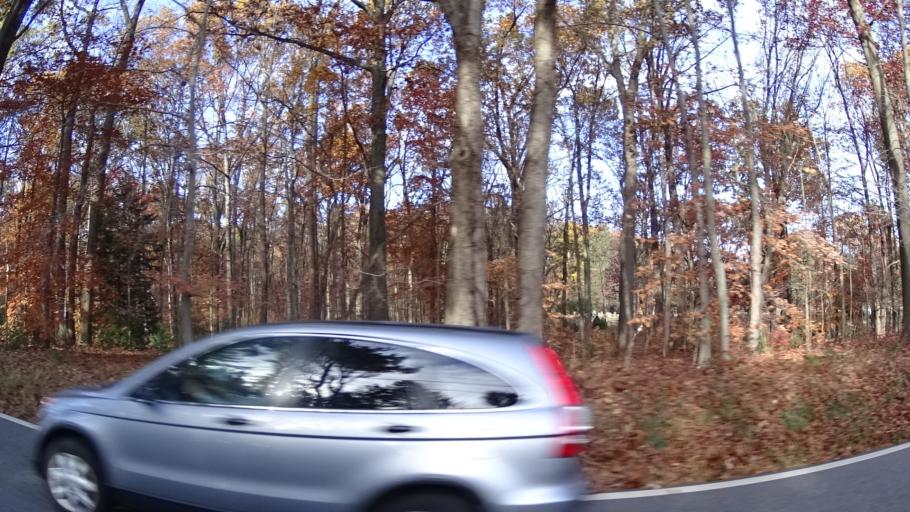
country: US
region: New Jersey
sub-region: Morris County
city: Morristown
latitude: 40.7466
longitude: -74.5055
